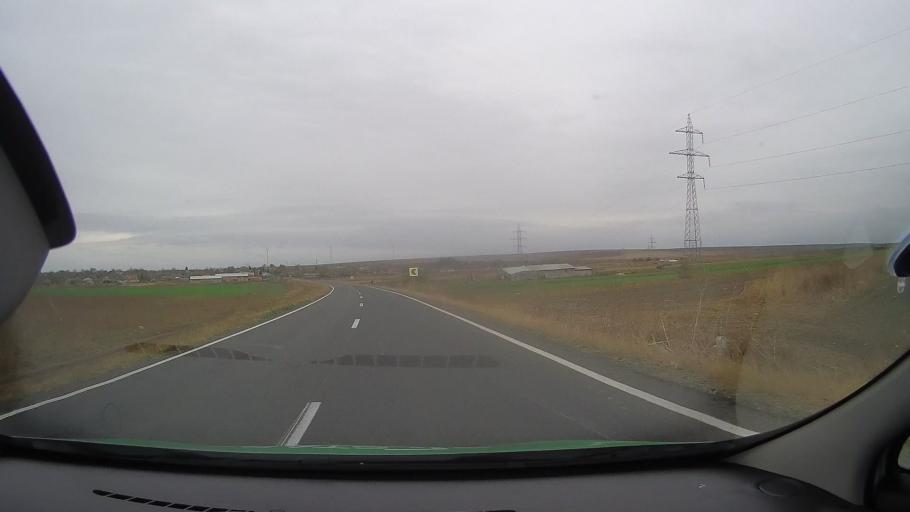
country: RO
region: Constanta
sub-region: Comuna Nicolae Balcescu
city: Dorobantu
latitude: 44.4150
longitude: 28.3167
